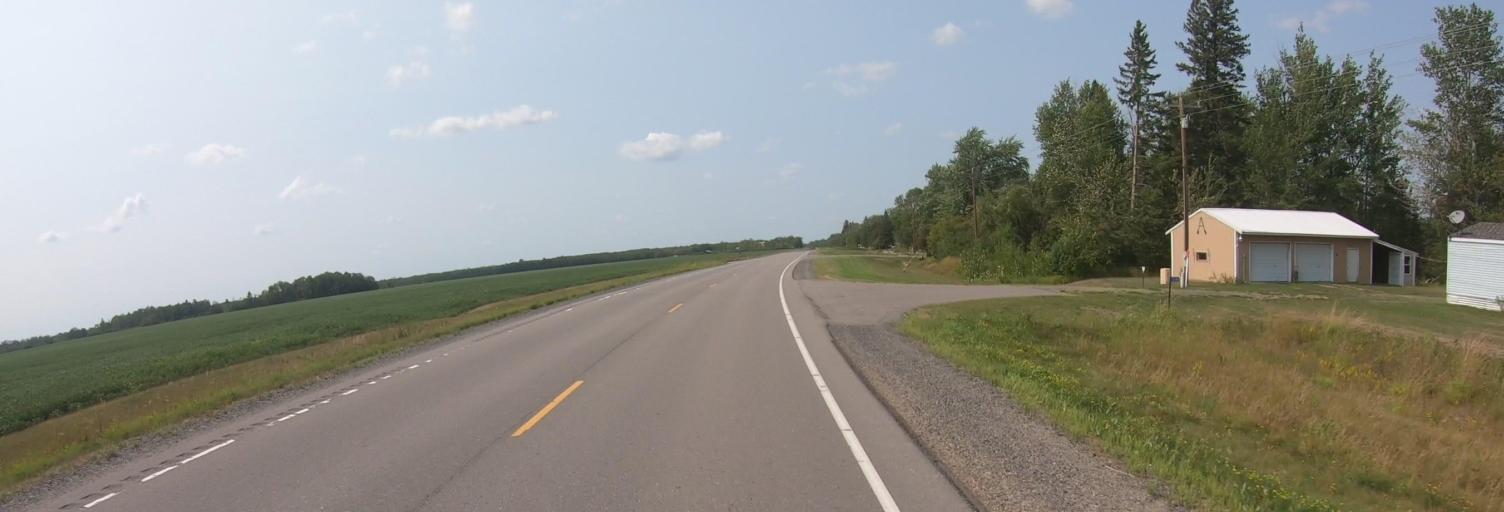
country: US
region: Minnesota
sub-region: Lake of the Woods County
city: Baudette
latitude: 48.6909
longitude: -94.4546
